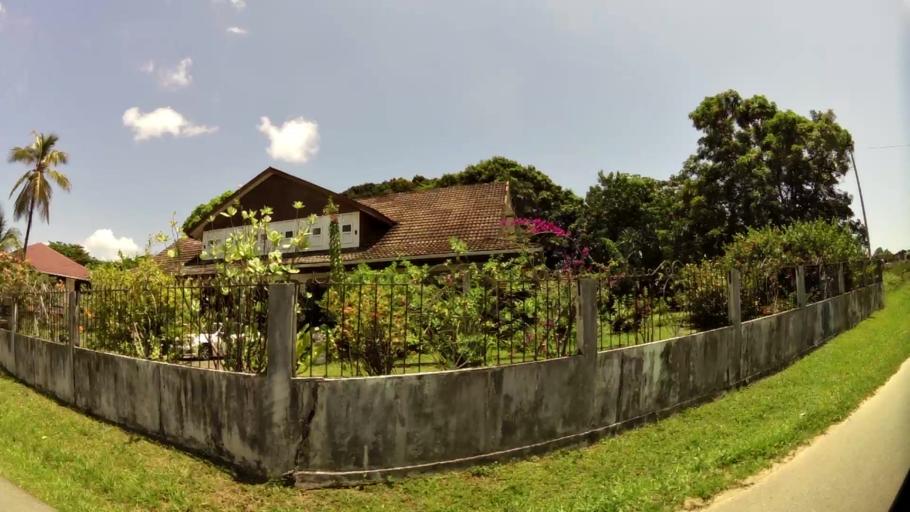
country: GF
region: Guyane
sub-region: Guyane
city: Cayenne
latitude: 4.8949
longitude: -52.3381
